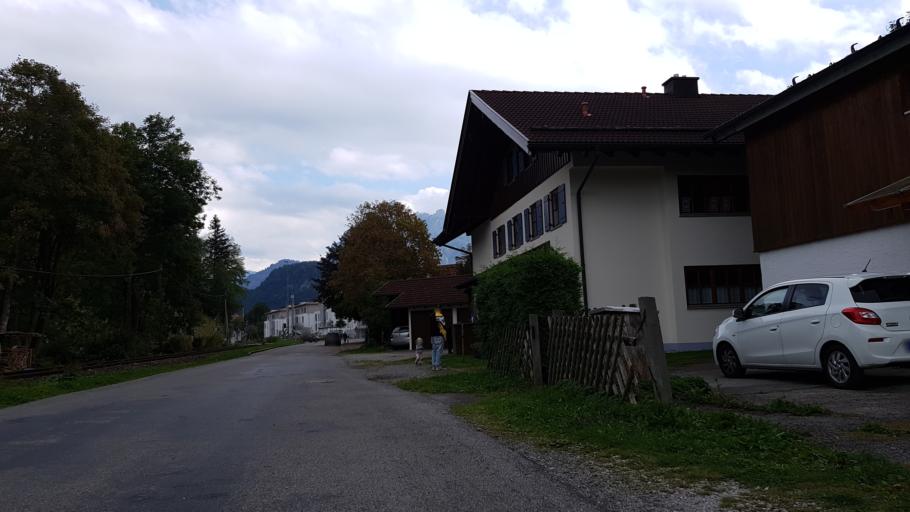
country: DE
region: Bavaria
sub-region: Swabia
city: Fuessen
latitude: 47.5725
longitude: 10.6911
